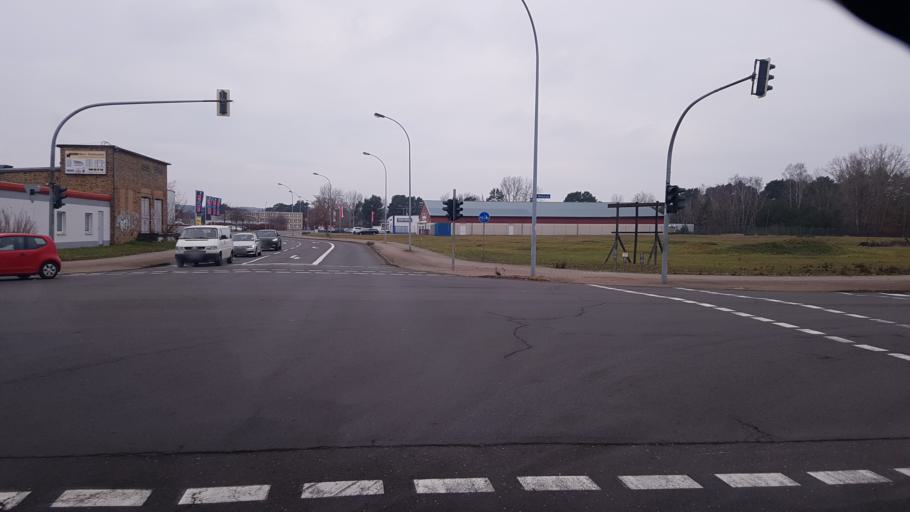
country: DE
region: Brandenburg
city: Eisenhuettenstadt
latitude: 52.1544
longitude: 14.6344
